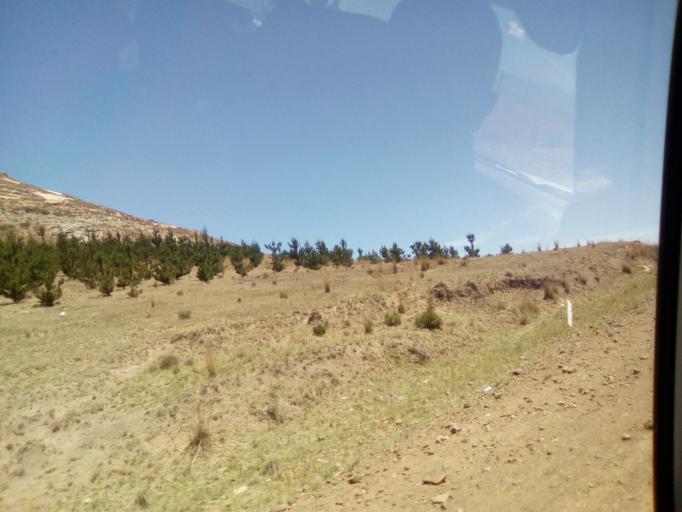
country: LS
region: Qacha's Nek
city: Qacha's Nek
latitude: -30.0379
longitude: 28.6814
